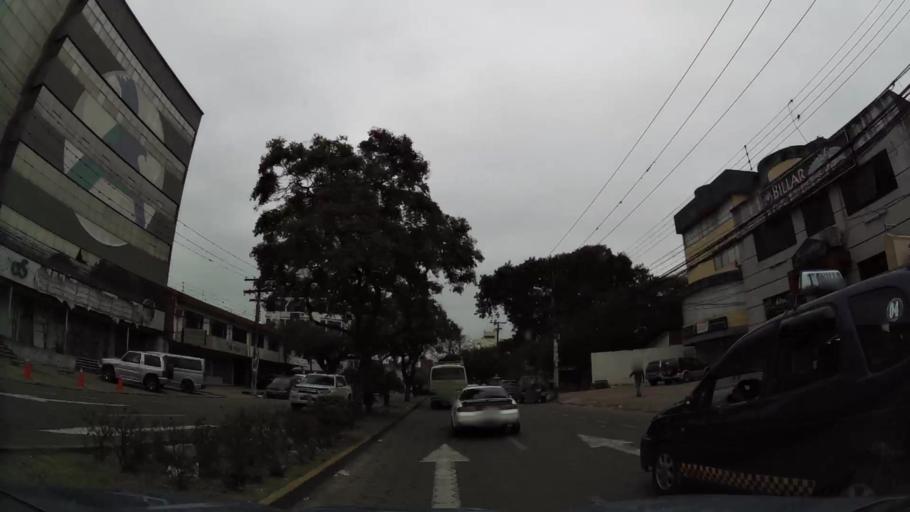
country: BO
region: Santa Cruz
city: Santa Cruz de la Sierra
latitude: -17.7929
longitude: -63.1841
